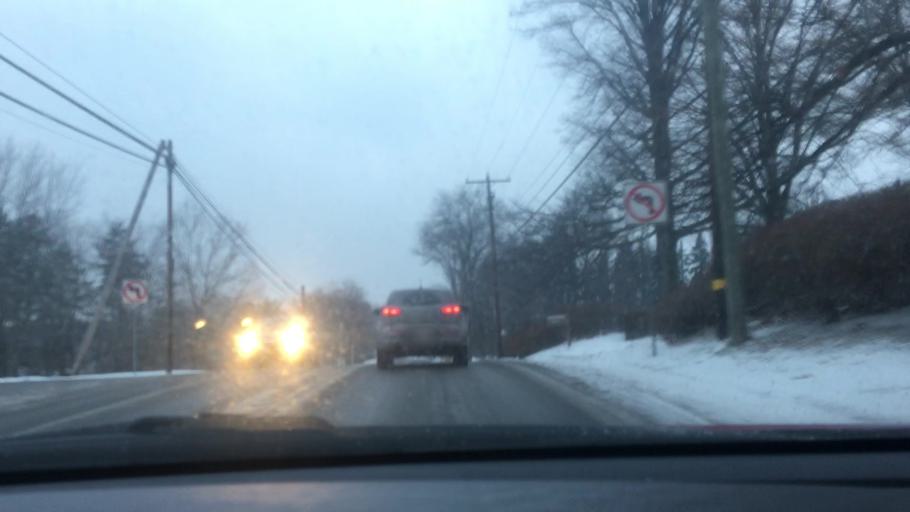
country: US
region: Pennsylvania
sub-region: Allegheny County
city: Baldwin
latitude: 40.3362
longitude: -80.0062
